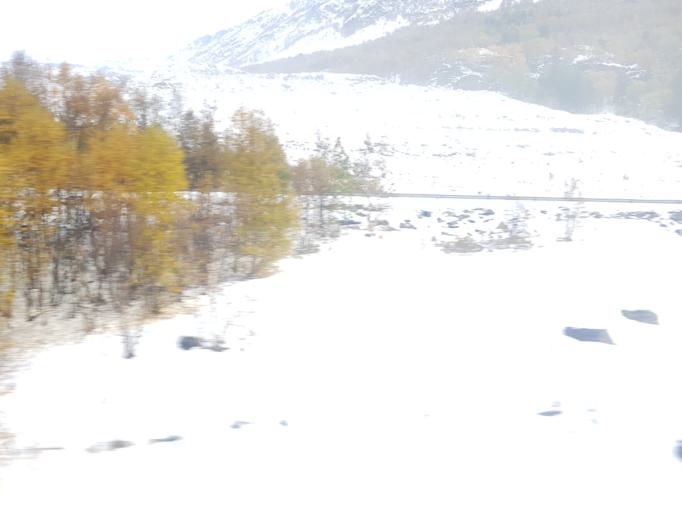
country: NO
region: Sor-Trondelag
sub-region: Oppdal
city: Oppdal
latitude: 62.4334
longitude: 9.6072
